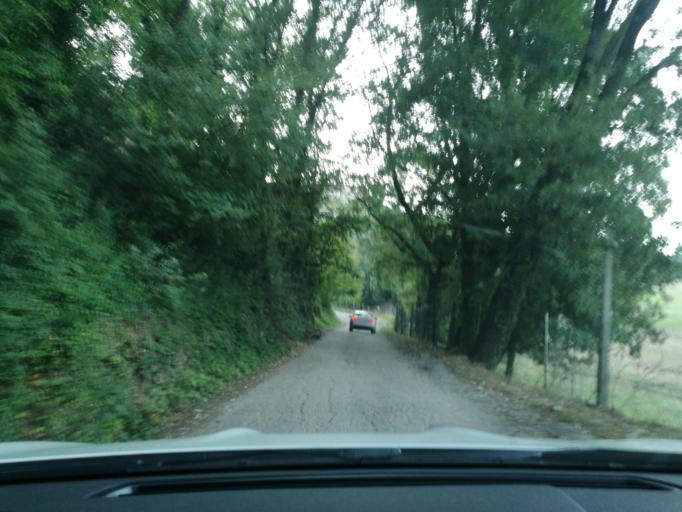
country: IT
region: Umbria
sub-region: Provincia di Terni
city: San Gemini
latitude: 42.6138
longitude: 12.5514
